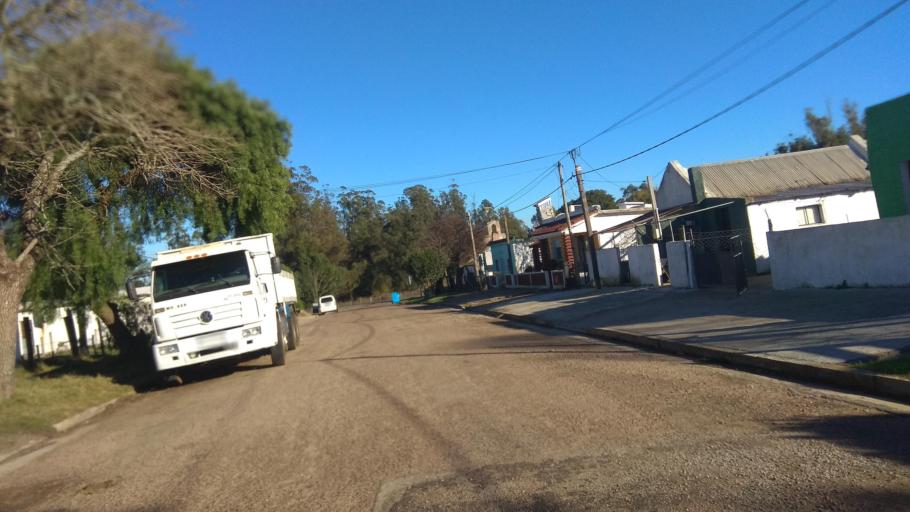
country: UY
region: Florida
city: Florida
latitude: -34.0950
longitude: -56.2389
